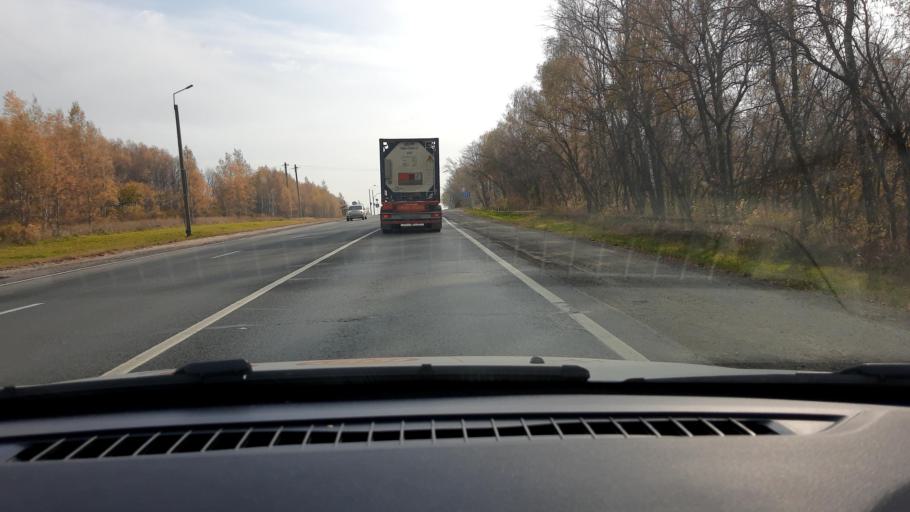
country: RU
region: Nizjnij Novgorod
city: Kstovo
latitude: 56.1159
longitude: 44.2778
